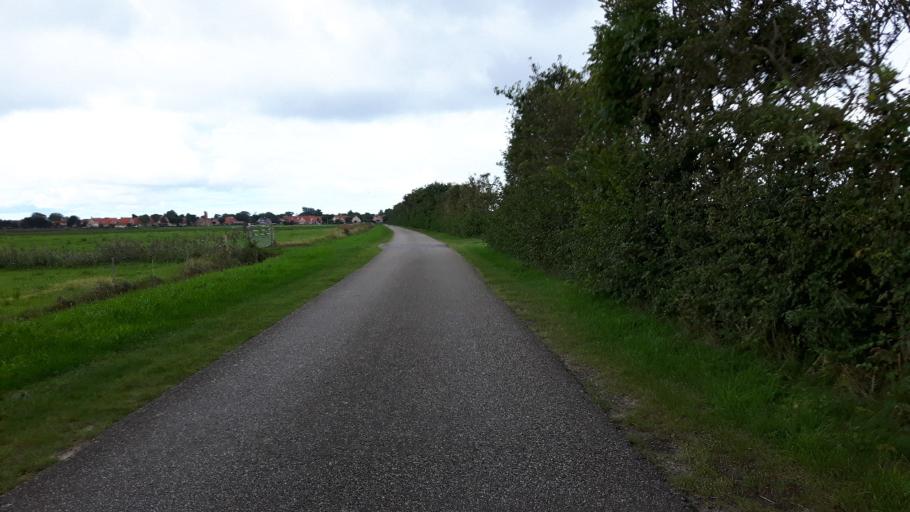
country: NL
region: Friesland
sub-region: Gemeente Ameland
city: Hollum
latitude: 53.4420
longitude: 5.6536
